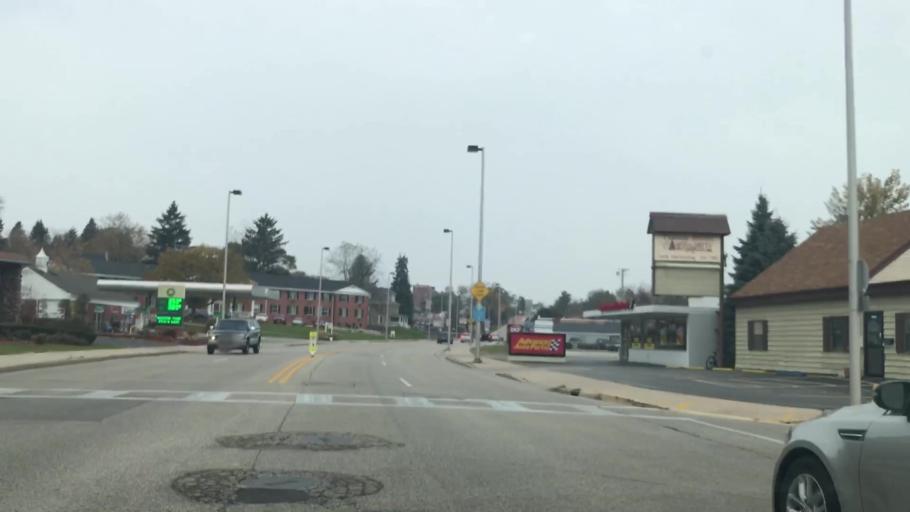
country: US
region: Wisconsin
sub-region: Waukesha County
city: Menomonee Falls
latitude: 43.1739
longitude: -88.1117
